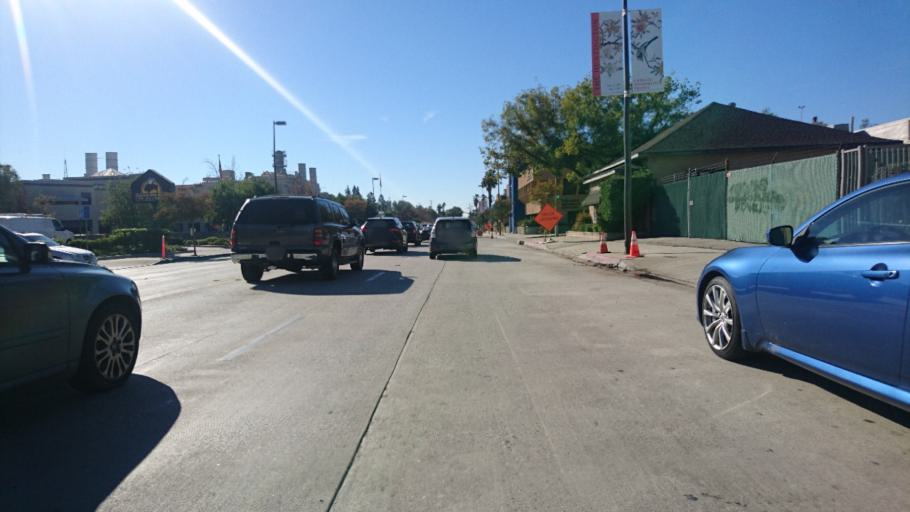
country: US
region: California
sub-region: Los Angeles County
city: South Pasadena
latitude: 34.1290
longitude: -118.1504
